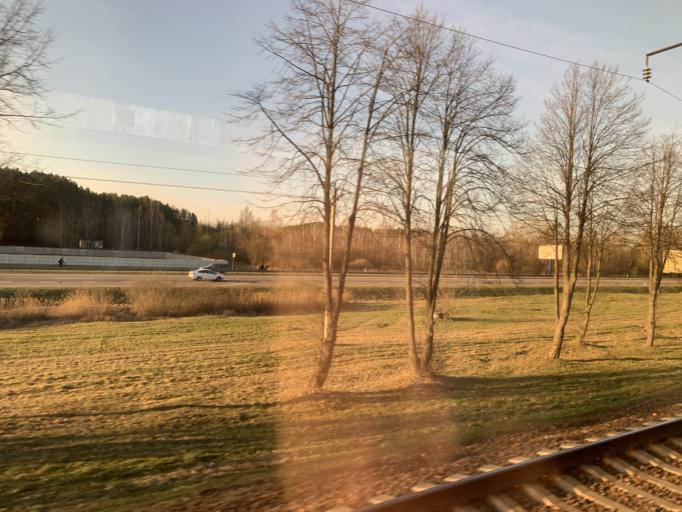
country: BY
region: Minsk
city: Zhdanovichy
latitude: 53.9497
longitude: 27.3875
